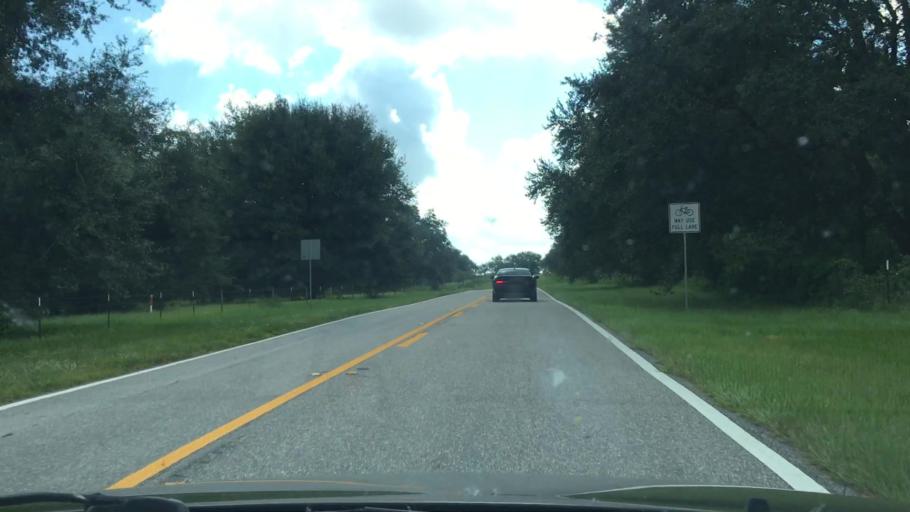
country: US
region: Florida
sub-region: Lake County
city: Montverde
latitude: 28.6464
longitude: -81.7148
